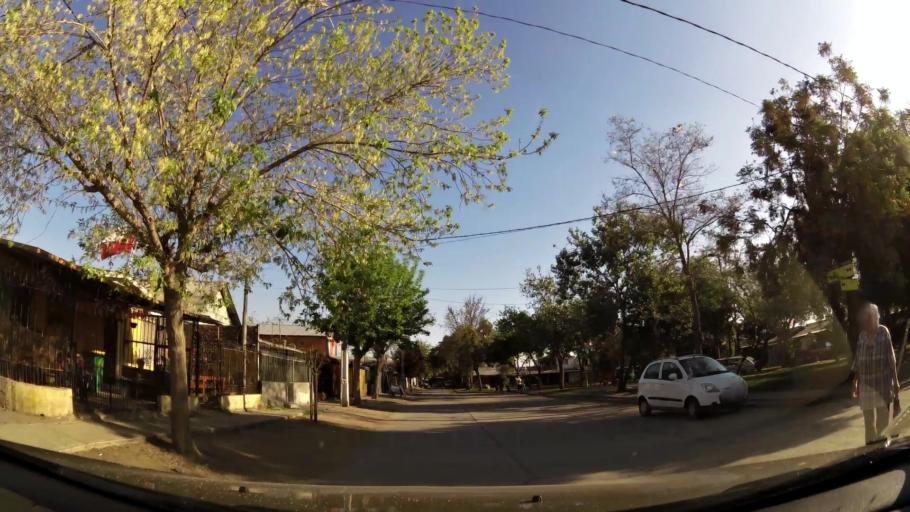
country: CL
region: Santiago Metropolitan
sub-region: Provincia de Santiago
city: La Pintana
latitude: -33.5791
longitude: -70.6607
